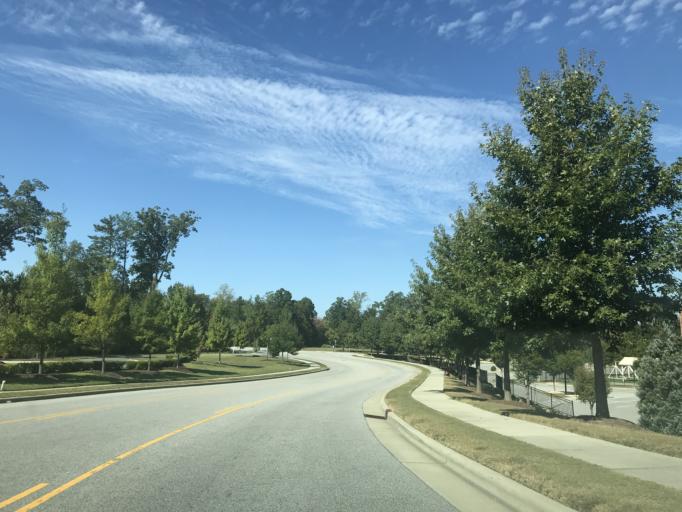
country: US
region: North Carolina
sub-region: Wake County
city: Knightdale
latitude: 35.8691
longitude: -78.5605
